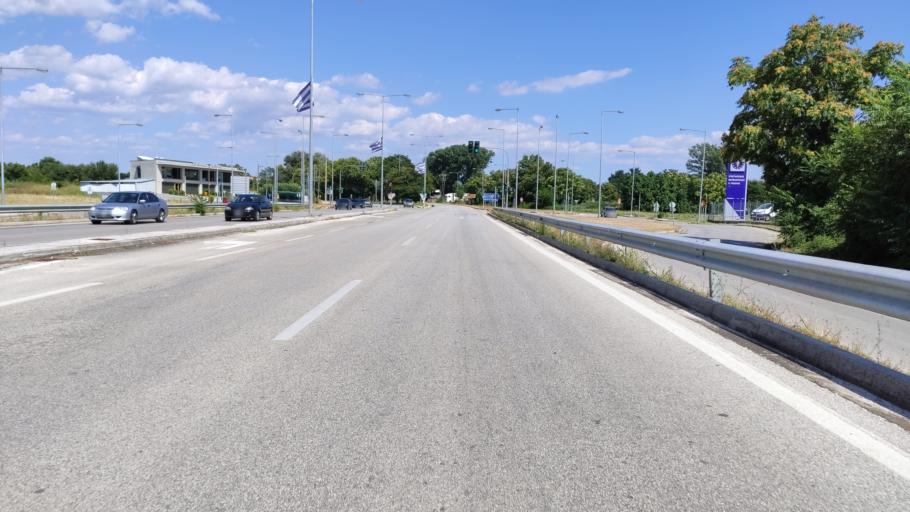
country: GR
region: East Macedonia and Thrace
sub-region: Nomos Rodopis
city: Komotini
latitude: 41.1136
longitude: 25.3851
